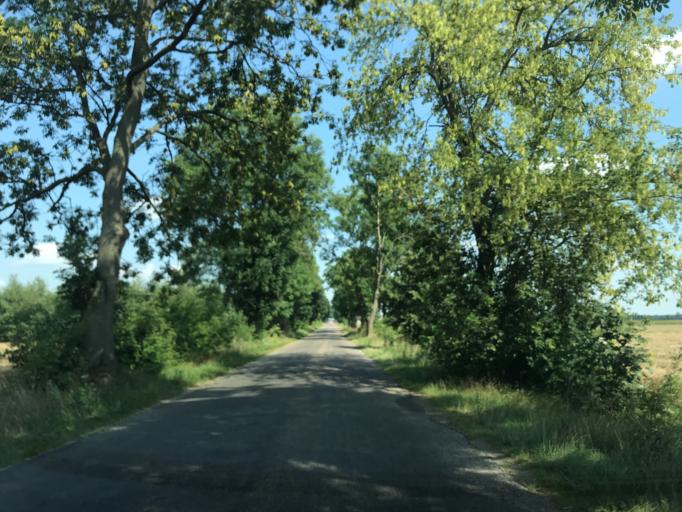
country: PL
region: Masovian Voivodeship
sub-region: Powiat zurominski
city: Lubowidz
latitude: 53.1738
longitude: 19.8833
